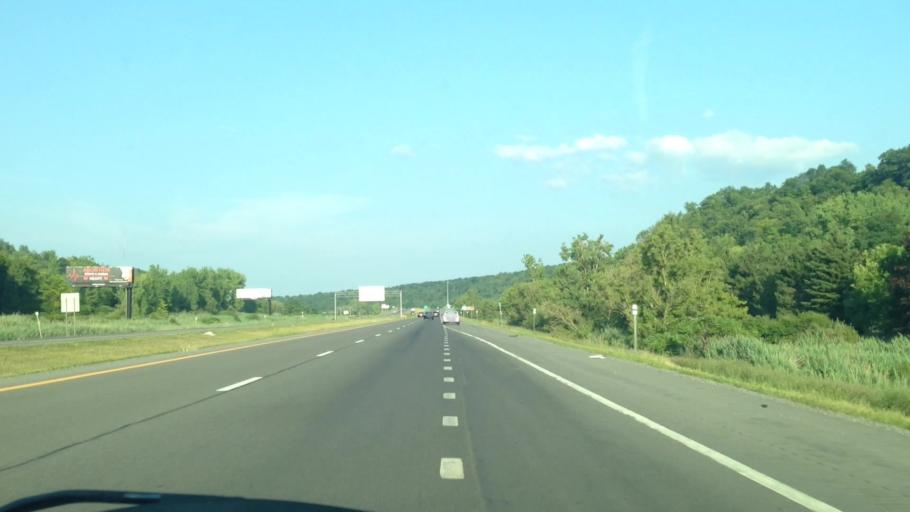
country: US
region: New York
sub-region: Onondaga County
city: Nedrow
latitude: 43.0056
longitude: -76.1140
